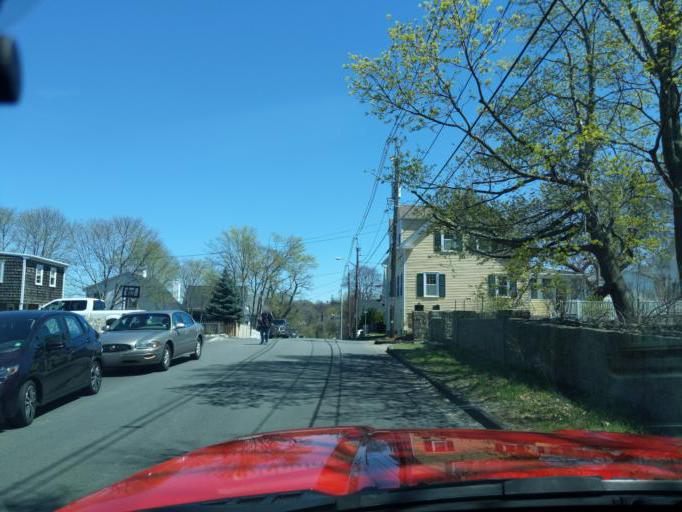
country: US
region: Massachusetts
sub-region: Essex County
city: Rockport
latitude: 42.6547
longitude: -70.6214
